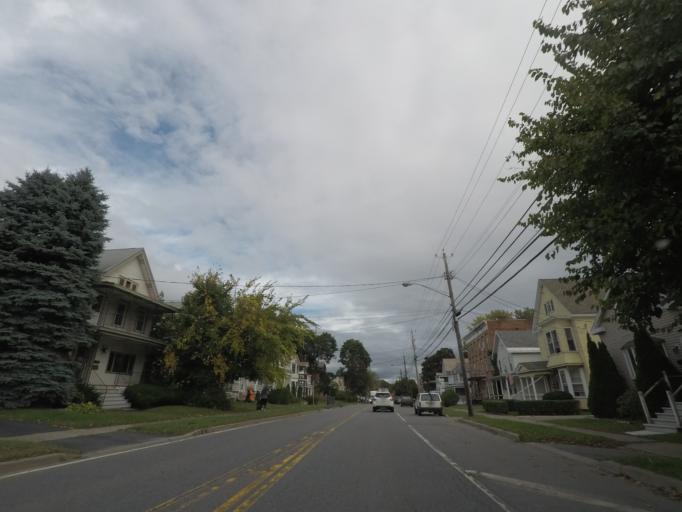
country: US
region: New York
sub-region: Albany County
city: Cohoes
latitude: 42.7831
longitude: -73.6955
